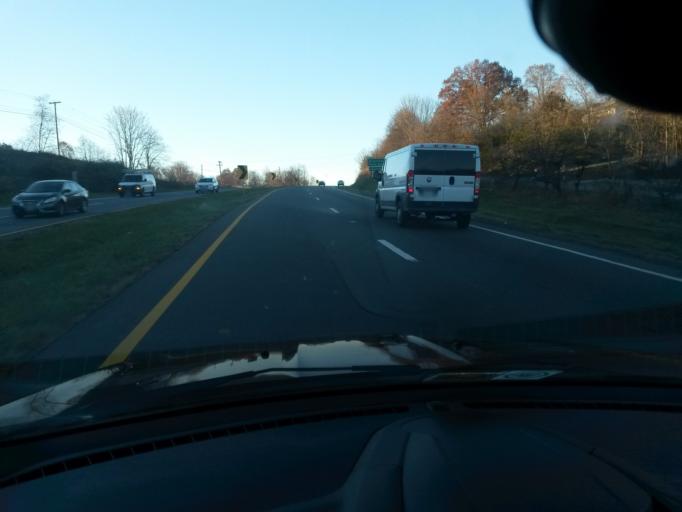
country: US
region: Virginia
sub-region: Franklin County
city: Rocky Mount
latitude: 37.0274
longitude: -79.8799
